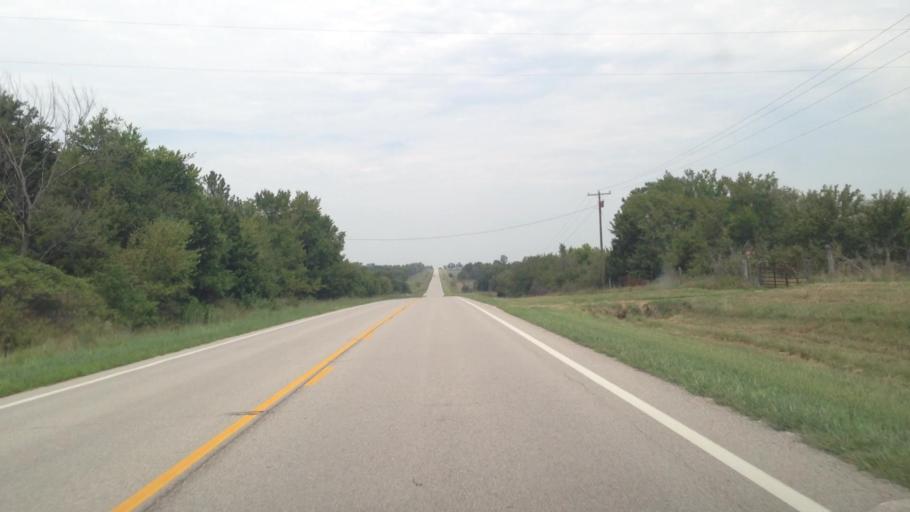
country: US
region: Kansas
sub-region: Neosho County
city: Erie
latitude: 37.6556
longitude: -95.2517
